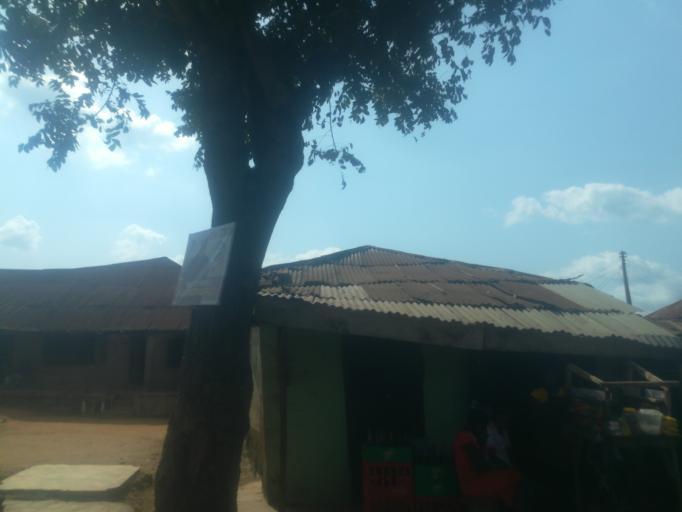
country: NG
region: Oyo
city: Moniya
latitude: 7.5278
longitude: 3.9116
